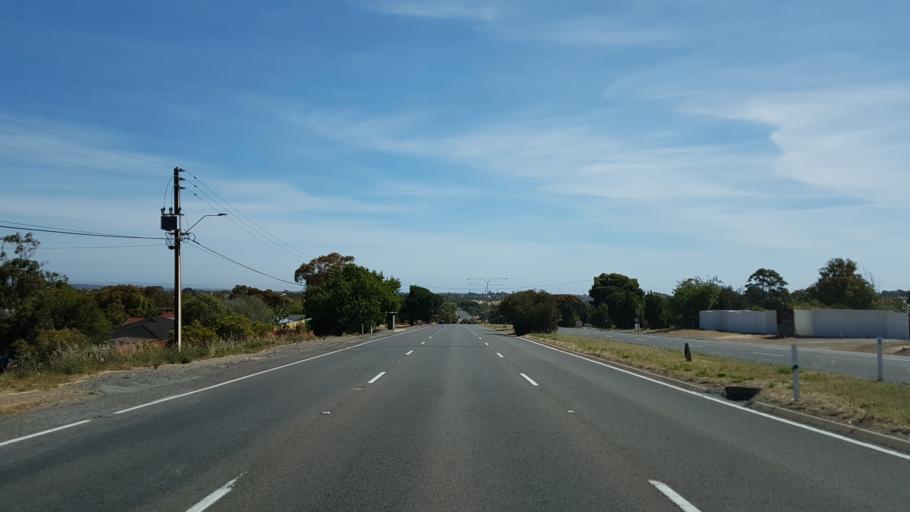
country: AU
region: South Australia
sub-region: Marion
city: Trott Park
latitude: -35.0730
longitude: 138.5526
